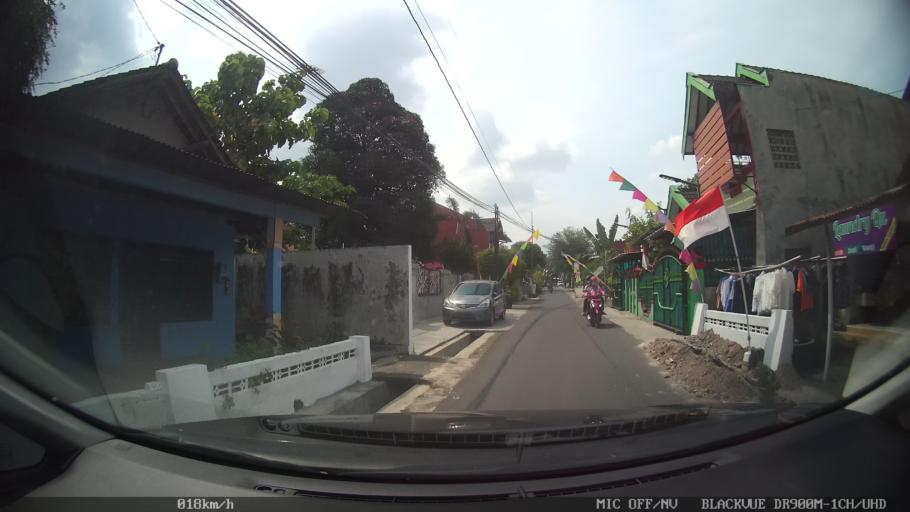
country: ID
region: Daerah Istimewa Yogyakarta
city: Depok
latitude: -7.7895
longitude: 110.4051
